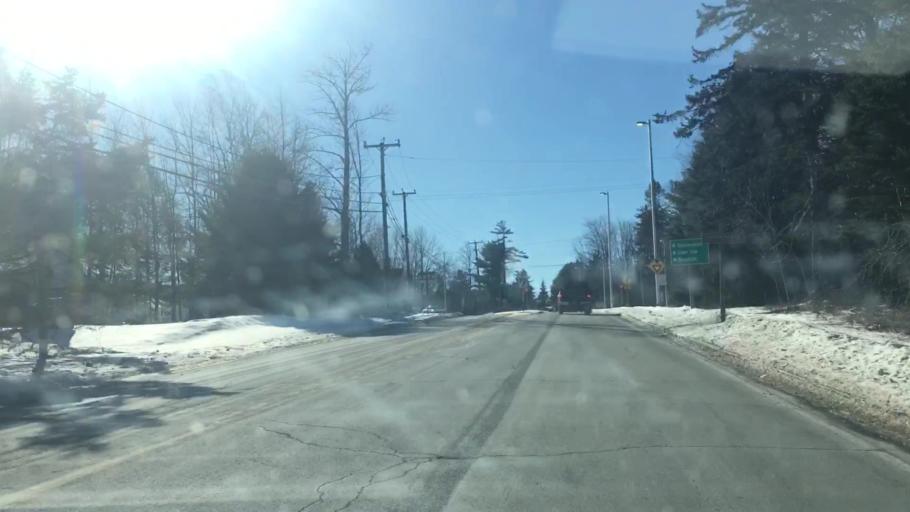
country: US
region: Maine
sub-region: Hancock County
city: Sedgwick
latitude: 44.4088
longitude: -68.5966
